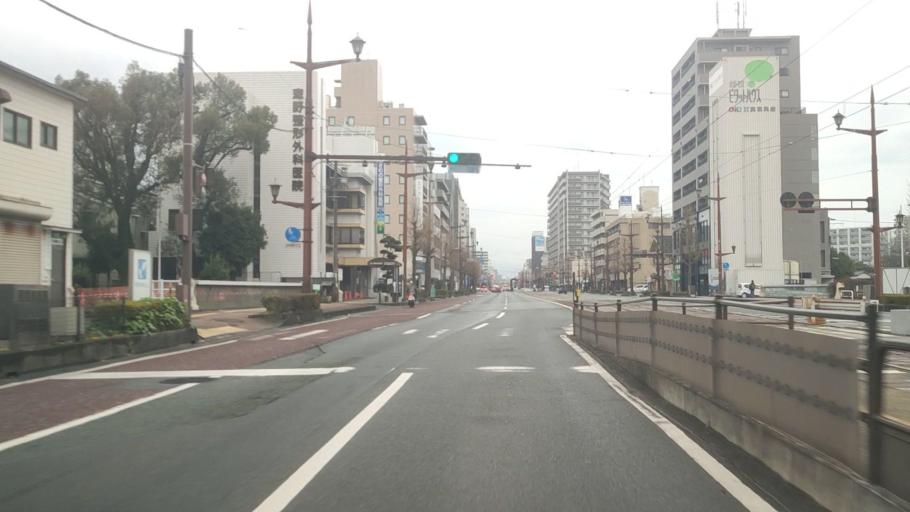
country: JP
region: Kumamoto
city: Kumamoto
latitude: 32.7883
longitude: 130.7348
